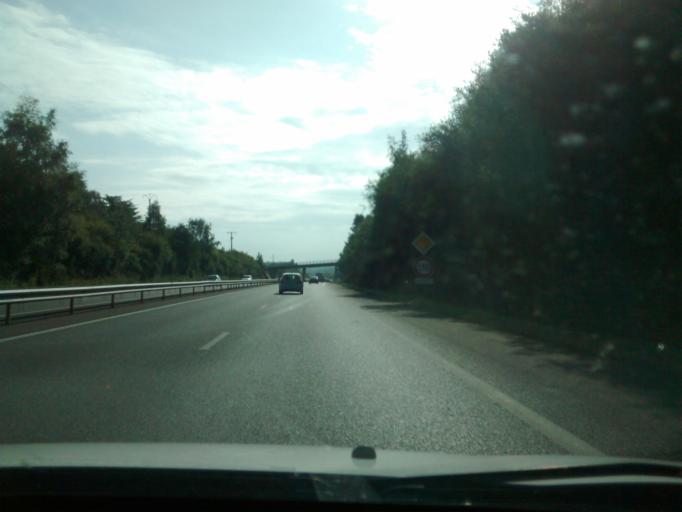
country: FR
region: Brittany
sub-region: Departement d'Ille-et-Vilaine
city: Erbree
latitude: 48.0899
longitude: -1.0889
